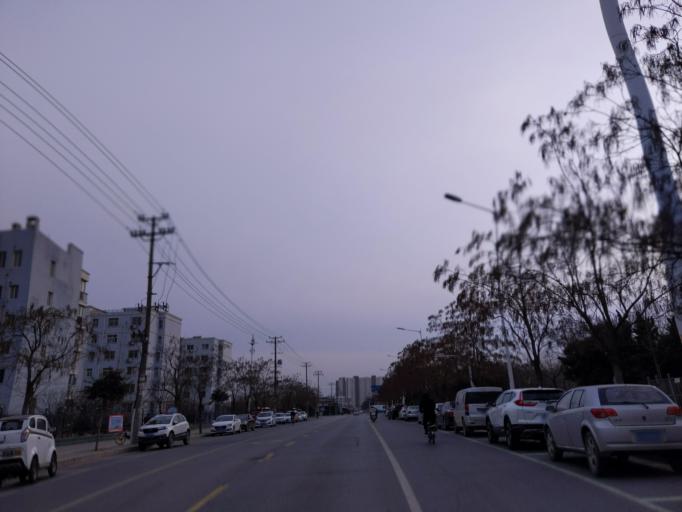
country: CN
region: Henan Sheng
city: Zhongyuanlu
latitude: 35.7587
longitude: 115.0405
